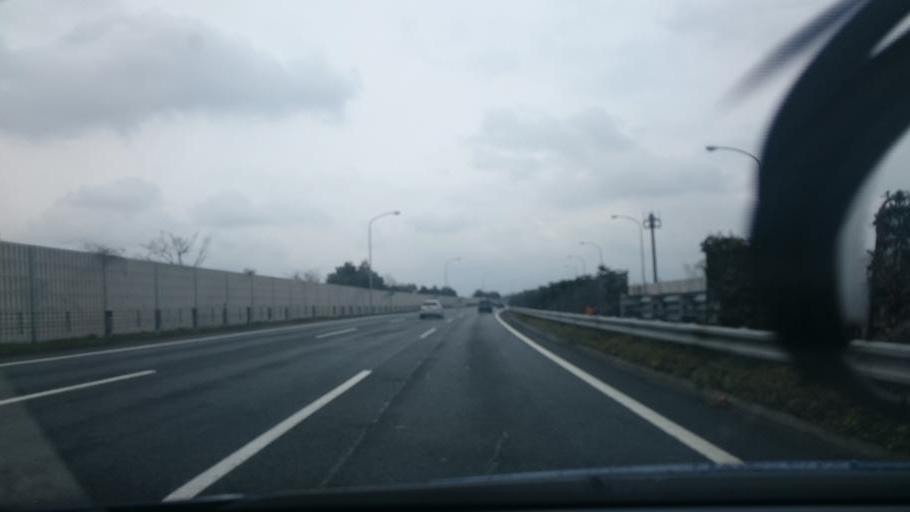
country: JP
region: Saitama
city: Ogawa
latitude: 36.0446
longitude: 139.3531
